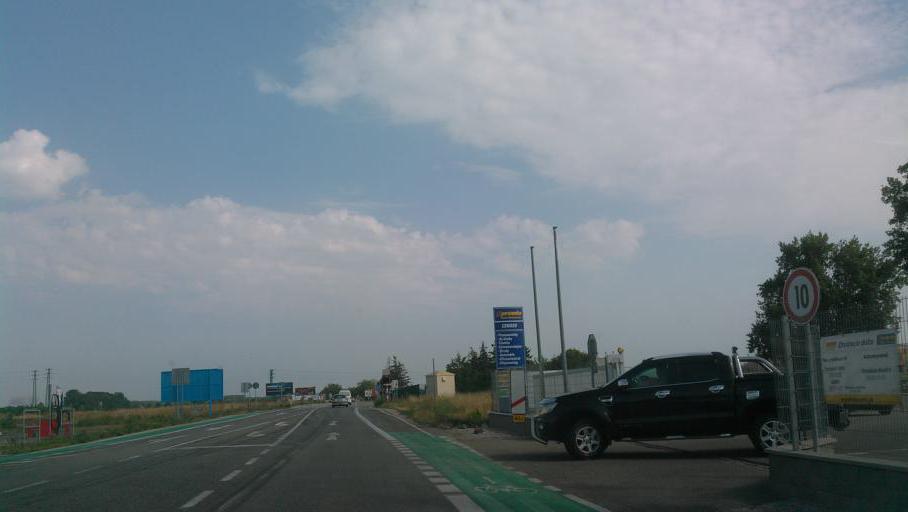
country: SK
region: Trnavsky
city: Dunajska Streda
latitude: 47.9876
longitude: 17.6328
